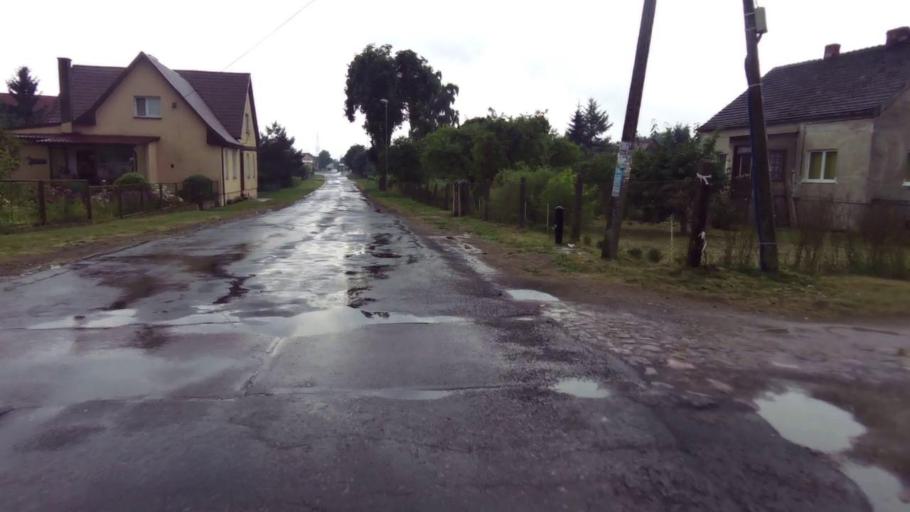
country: PL
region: West Pomeranian Voivodeship
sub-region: Powiat choszczenski
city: Recz
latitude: 53.2765
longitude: 15.4627
